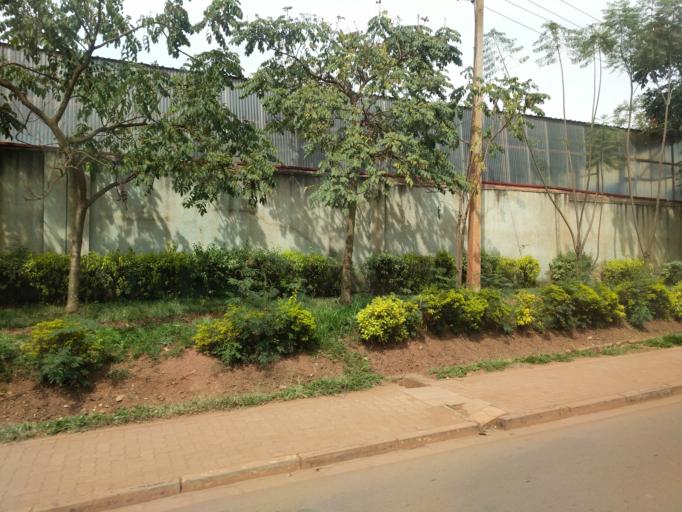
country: RW
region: Kigali
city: Kigali
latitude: -1.9751
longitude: 30.1070
